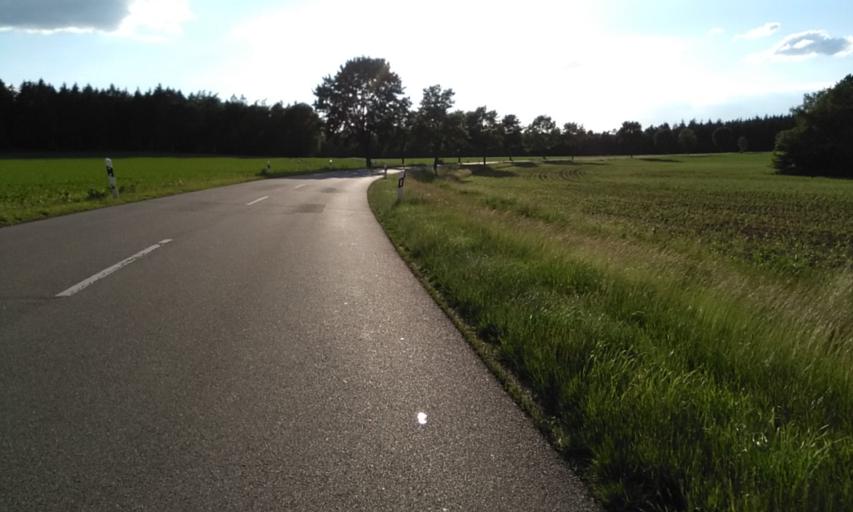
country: DE
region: Lower Saxony
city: Heeslingen
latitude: 53.3520
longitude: 9.3484
